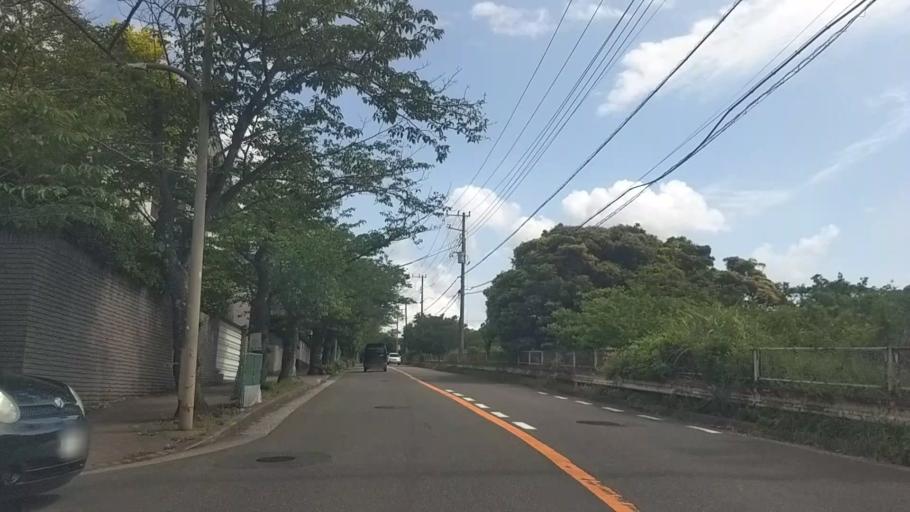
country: JP
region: Kanagawa
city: Zushi
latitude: 35.3103
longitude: 139.5766
